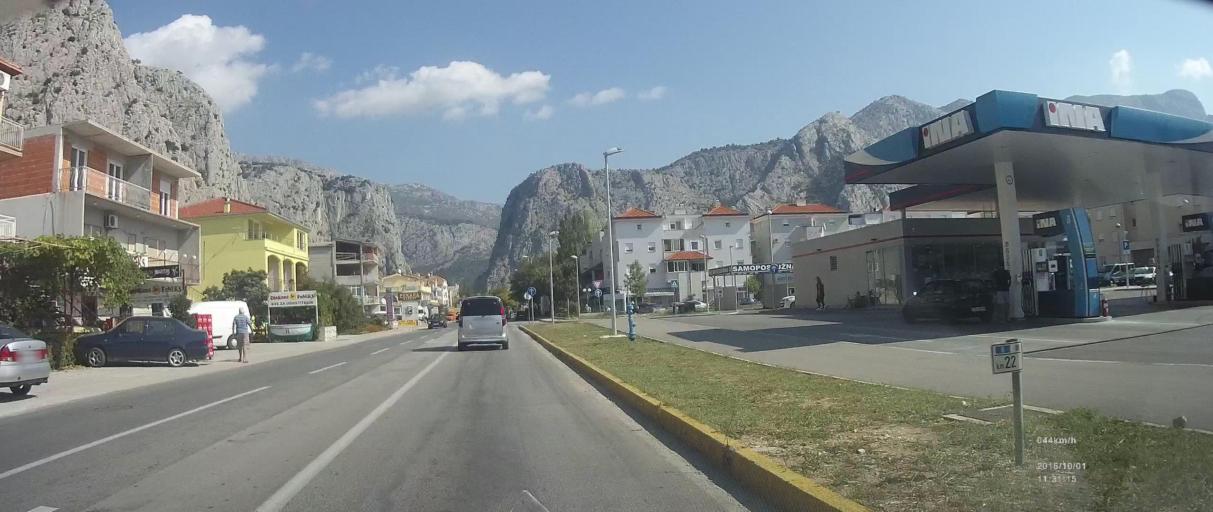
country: HR
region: Splitsko-Dalmatinska
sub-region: Grad Omis
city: Omis
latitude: 43.4429
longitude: 16.6831
